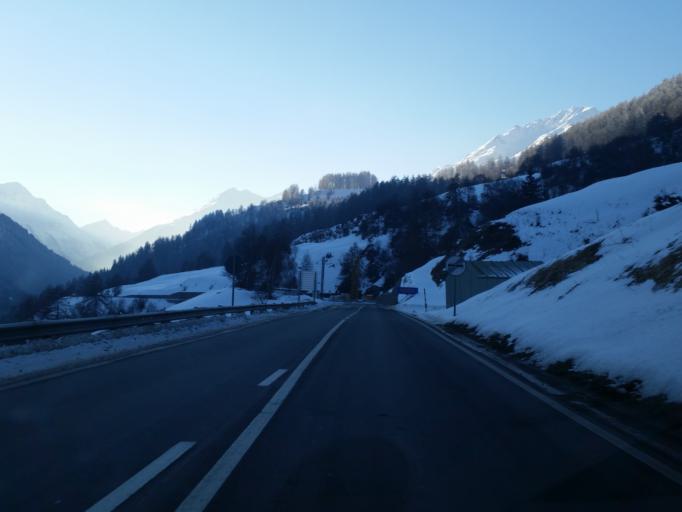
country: CH
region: Grisons
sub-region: Inn District
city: Zernez
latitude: 46.7748
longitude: 10.1870
